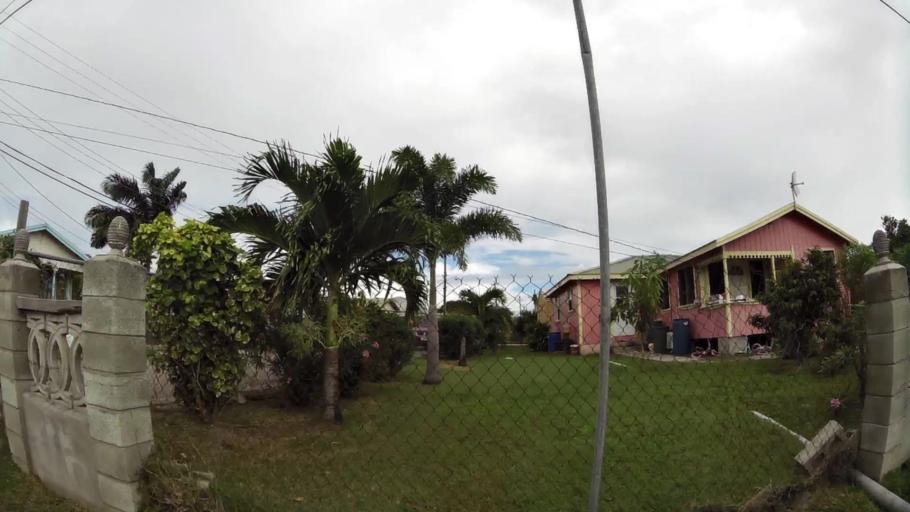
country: AG
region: Saint John
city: Potters Village
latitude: 17.0937
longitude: -61.8150
